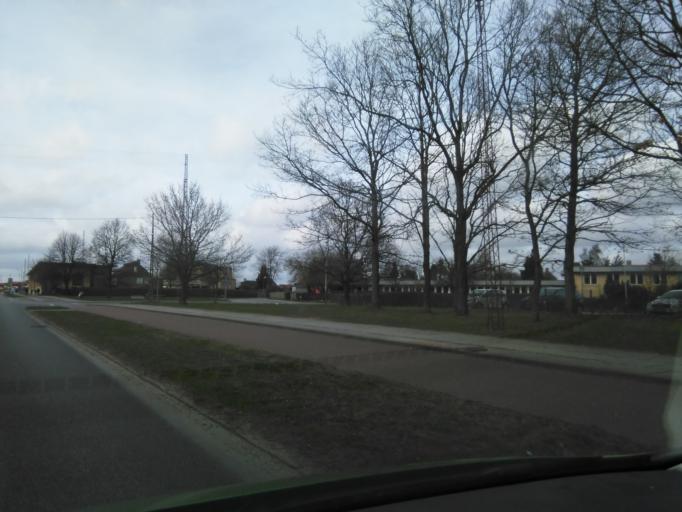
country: DK
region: Central Jutland
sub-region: Arhus Kommune
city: Arhus
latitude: 56.1743
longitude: 10.1817
